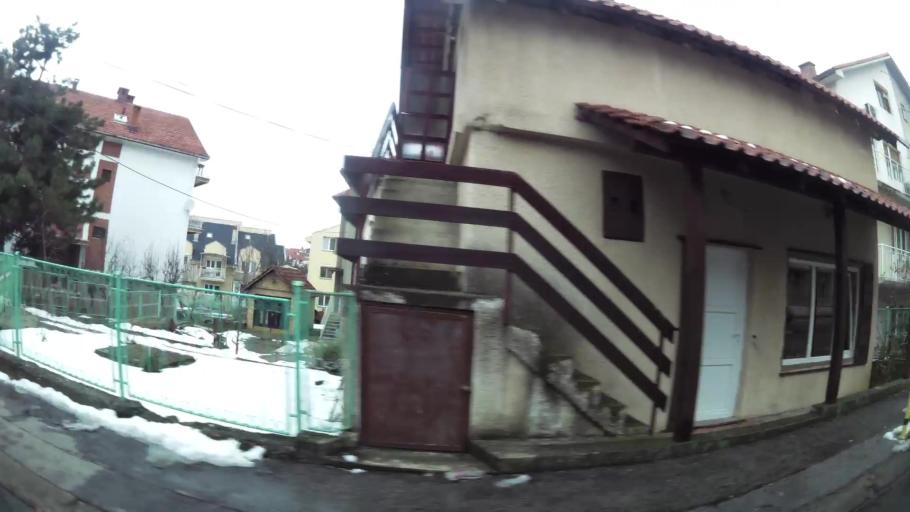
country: RS
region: Central Serbia
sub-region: Belgrade
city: Rakovica
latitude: 44.7548
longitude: 20.4192
